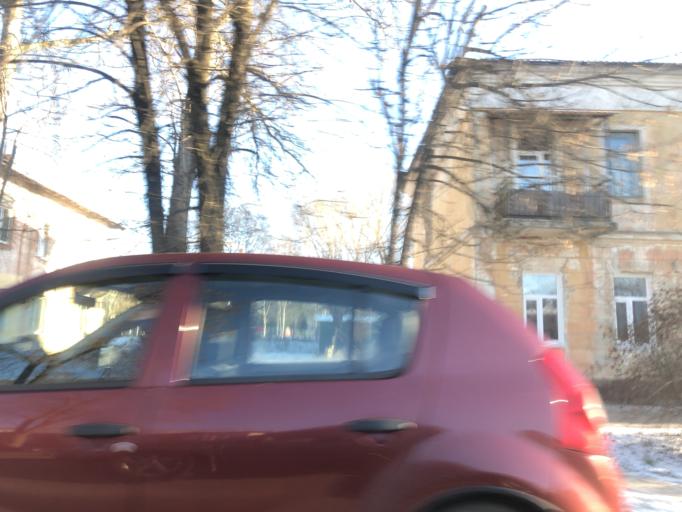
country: RU
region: Tverskaya
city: Rzhev
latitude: 56.2600
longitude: 34.3504
